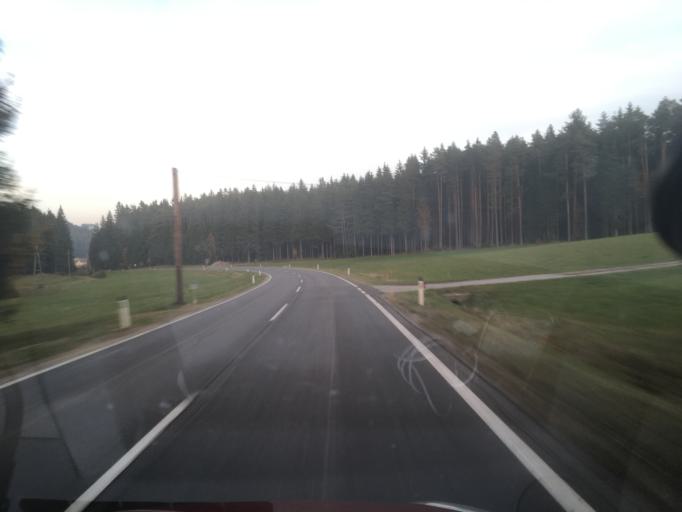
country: AT
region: Lower Austria
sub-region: Politischer Bezirk Zwettl
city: Langschlag
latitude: 48.5788
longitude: 14.8062
